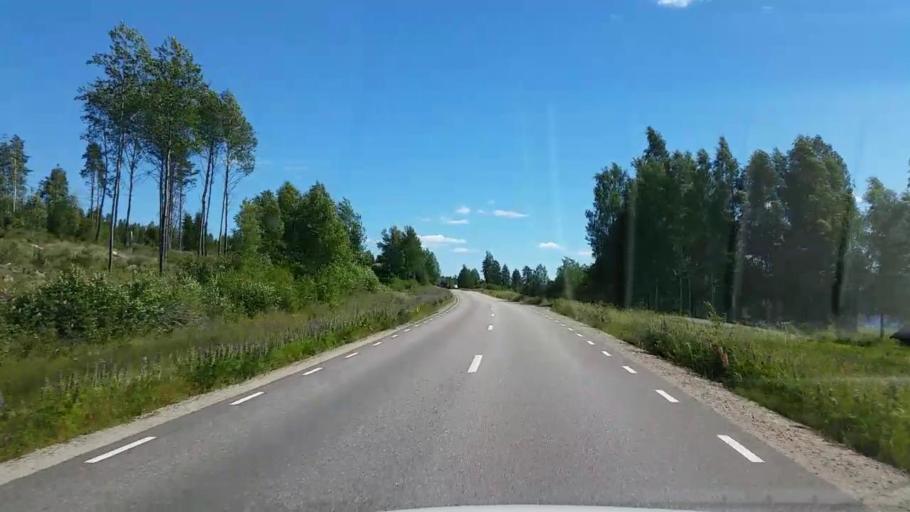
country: SE
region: Gaevleborg
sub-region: Ovanakers Kommun
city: Edsbyn
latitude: 61.4152
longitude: 15.7559
